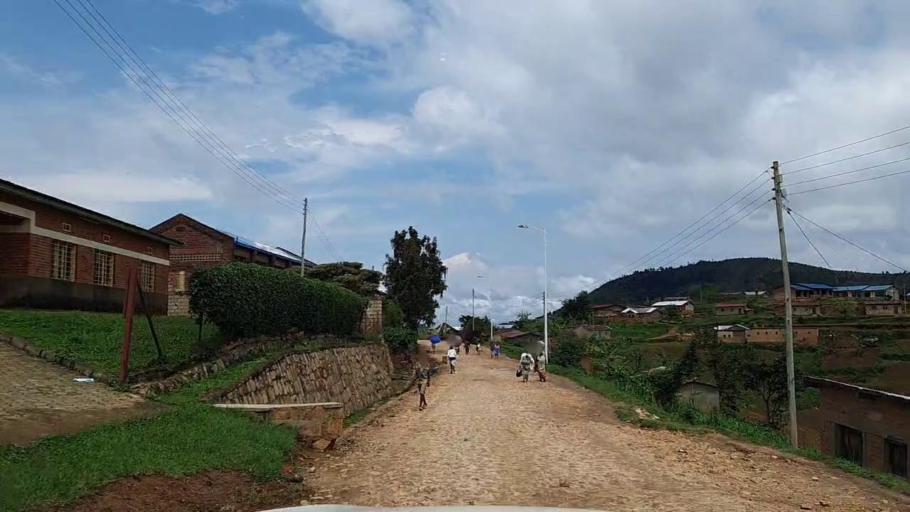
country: RW
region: Southern Province
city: Gikongoro
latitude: -2.3317
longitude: 29.5283
